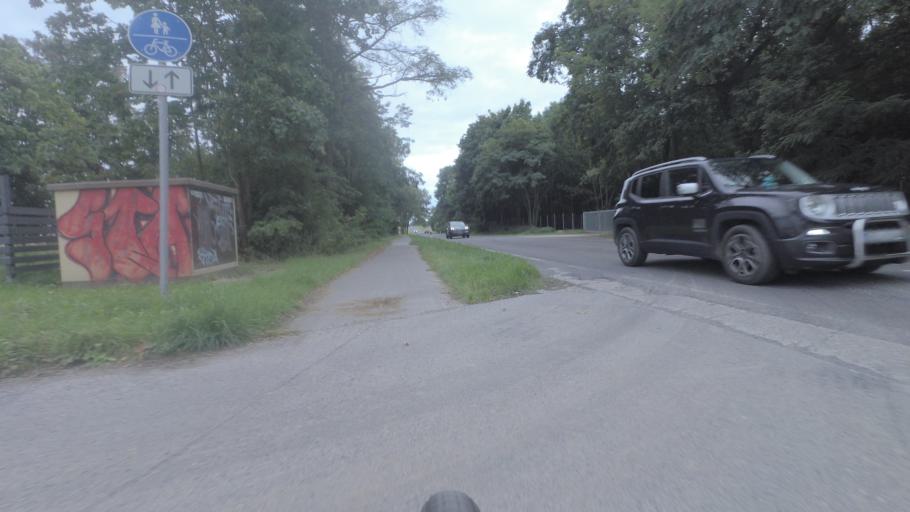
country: DE
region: Brandenburg
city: Werneuchen
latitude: 52.6092
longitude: 13.6821
